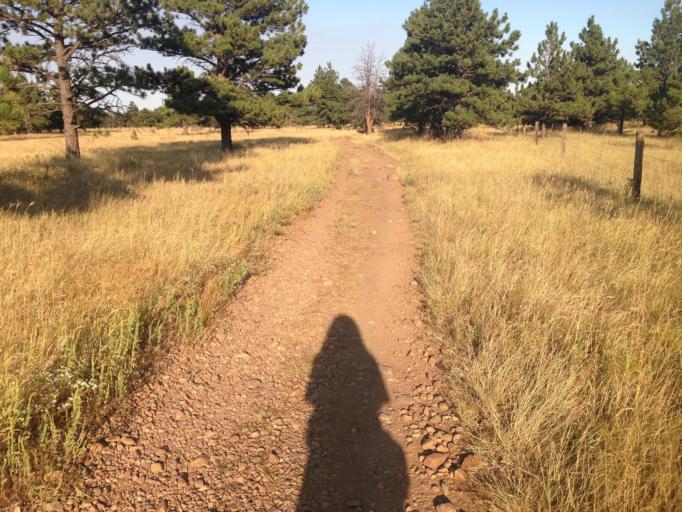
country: US
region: Colorado
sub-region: Boulder County
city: Superior
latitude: 39.9140
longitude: -105.2564
